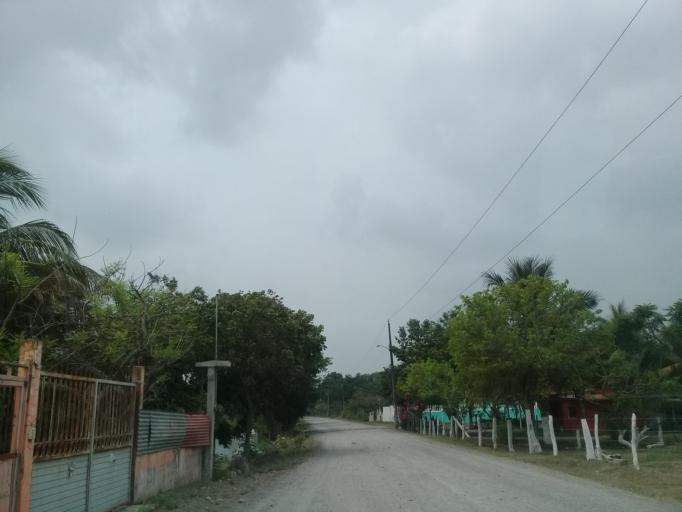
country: MX
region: Veracruz
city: El Tejar
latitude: 19.0579
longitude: -96.1983
